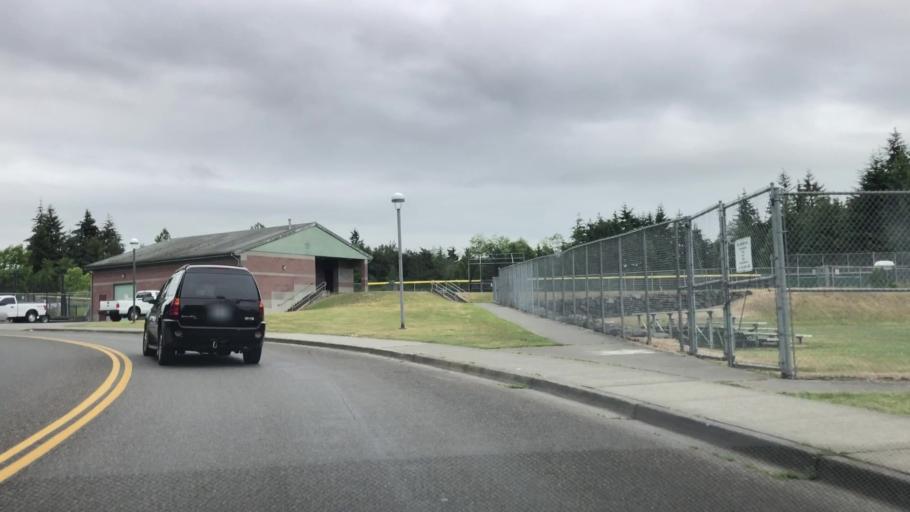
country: US
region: Washington
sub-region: Snohomish County
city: Mill Creek
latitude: 47.8734
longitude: -122.2059
